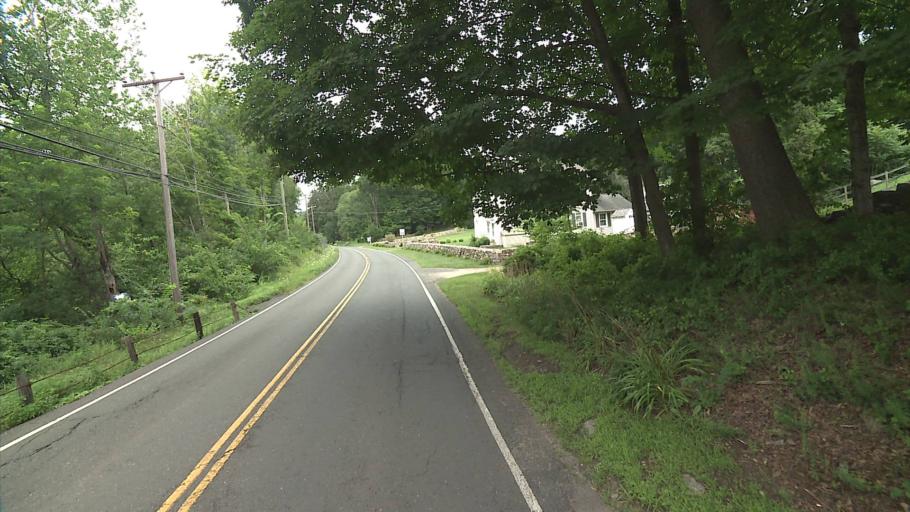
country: US
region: Connecticut
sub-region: Litchfield County
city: New Milford
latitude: 41.5486
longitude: -73.3335
